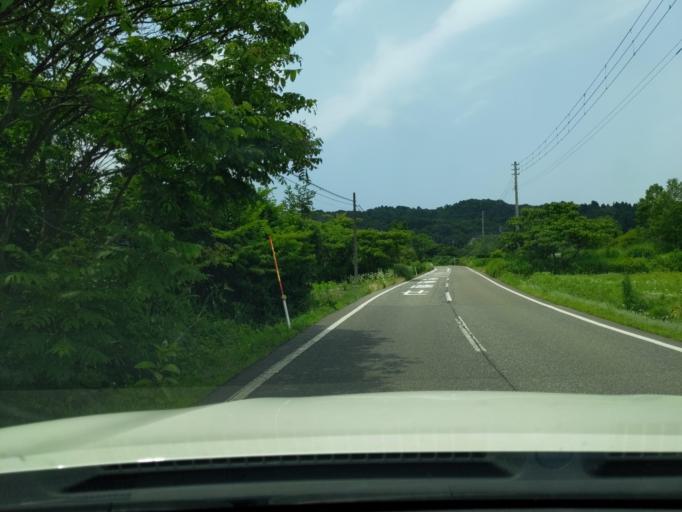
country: JP
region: Niigata
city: Kashiwazaki
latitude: 37.3325
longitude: 138.5590
